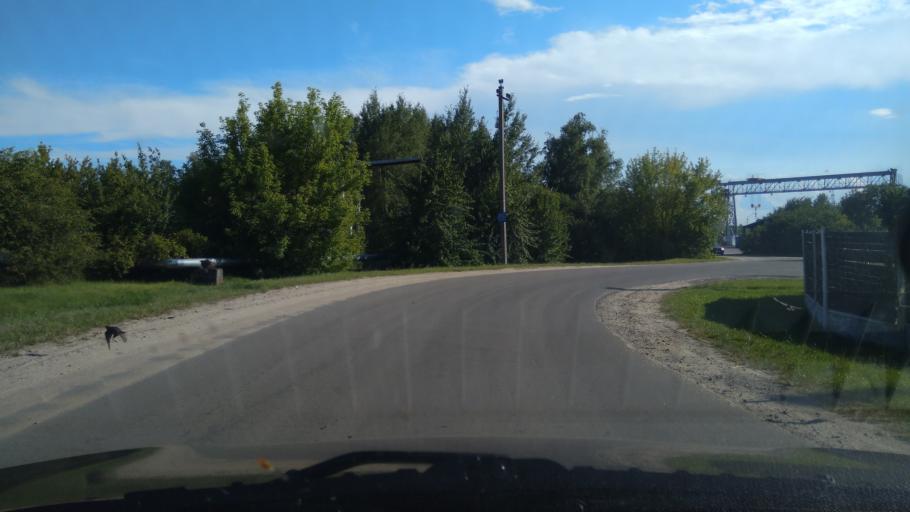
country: BY
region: Brest
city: Byelaazyorsk
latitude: 52.4586
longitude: 25.1892
